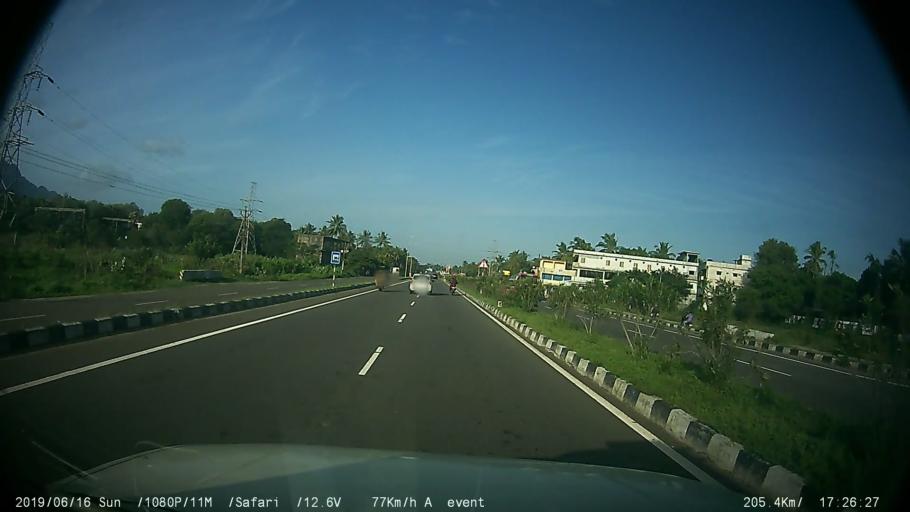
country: IN
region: Kerala
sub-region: Palakkad district
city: Palakkad
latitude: 10.7990
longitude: 76.7516
